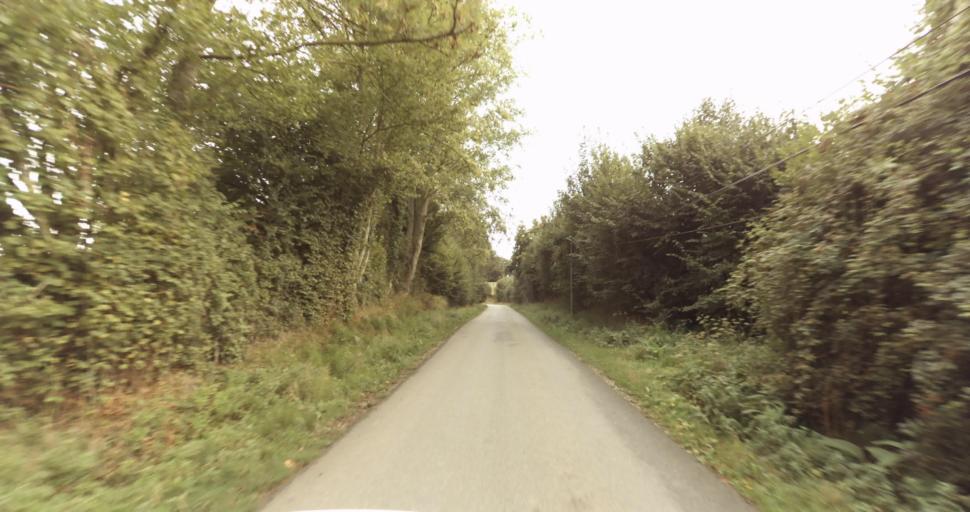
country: FR
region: Lower Normandy
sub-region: Departement du Calvados
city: Livarot
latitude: 48.9219
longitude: 0.0942
